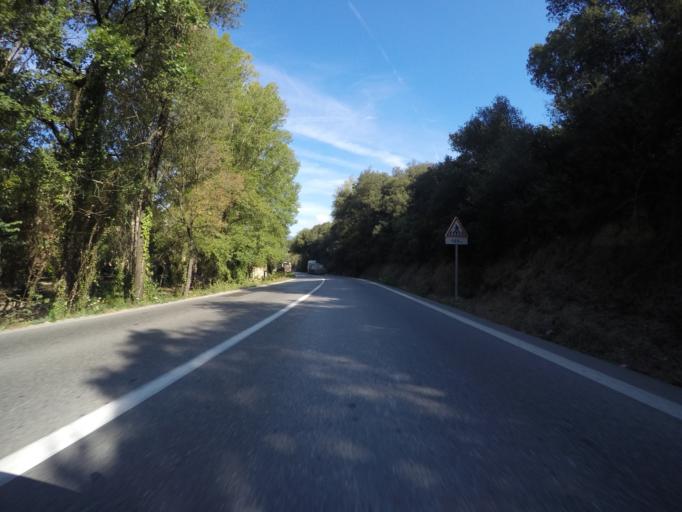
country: FR
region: Provence-Alpes-Cote d'Azur
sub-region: Departement des Alpes-Maritimes
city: Villeneuve-Loubet
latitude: 43.6589
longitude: 7.1046
